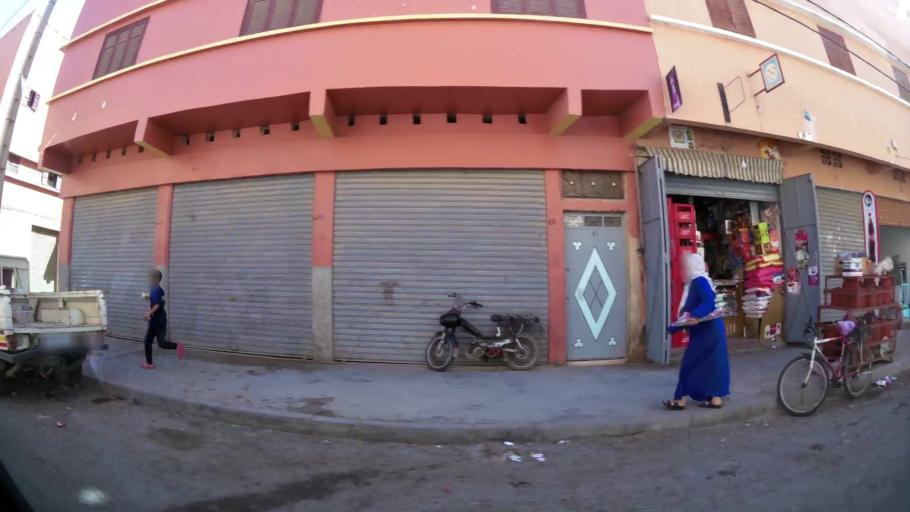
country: MA
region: Souss-Massa-Draa
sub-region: Inezgane-Ait Mellou
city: Inezgane
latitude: 30.3445
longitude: -9.5061
